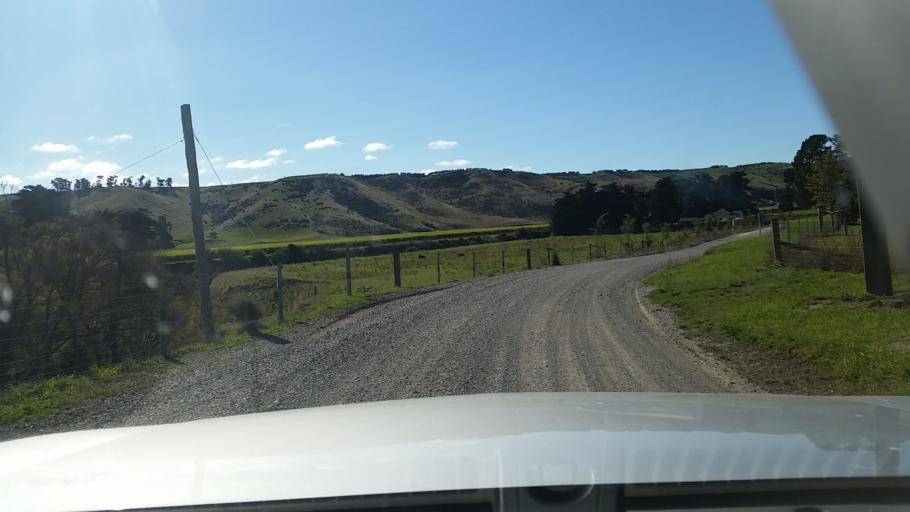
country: NZ
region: Marlborough
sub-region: Marlborough District
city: Blenheim
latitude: -41.6723
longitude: 174.1471
